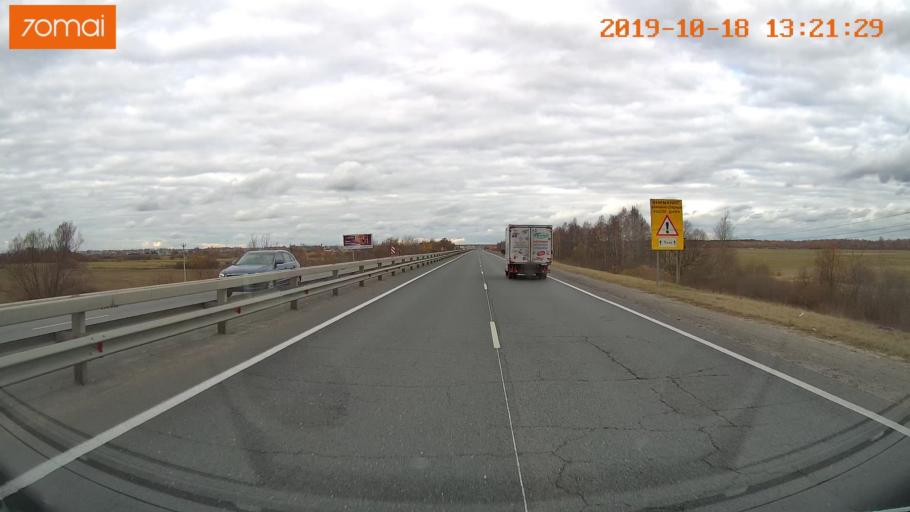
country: RU
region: Rjazan
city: Polyany
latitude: 54.6961
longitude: 39.8396
